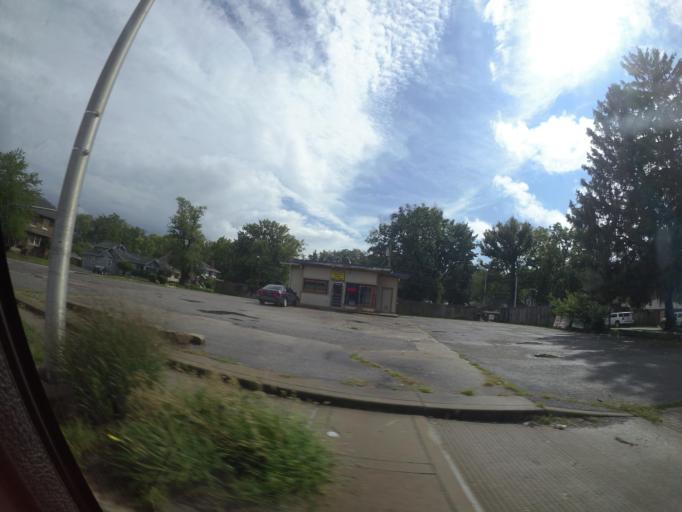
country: US
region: Indiana
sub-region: Marion County
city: Broad Ripple
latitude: 39.8250
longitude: -86.1429
